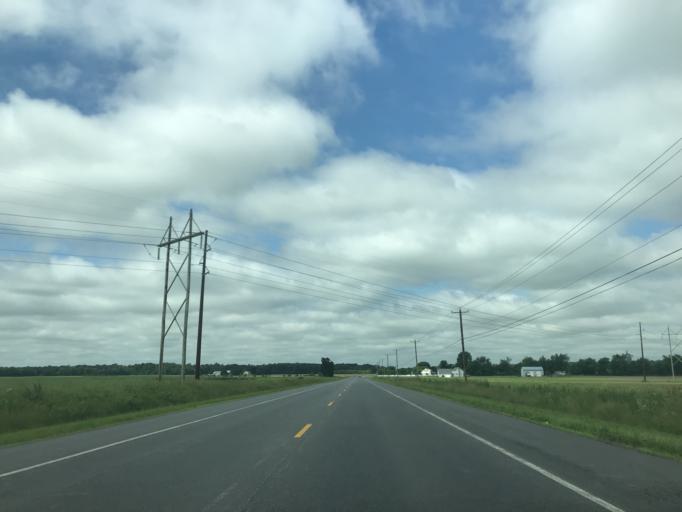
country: US
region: Maryland
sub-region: Caroline County
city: Ridgely
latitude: 38.9308
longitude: -75.9078
